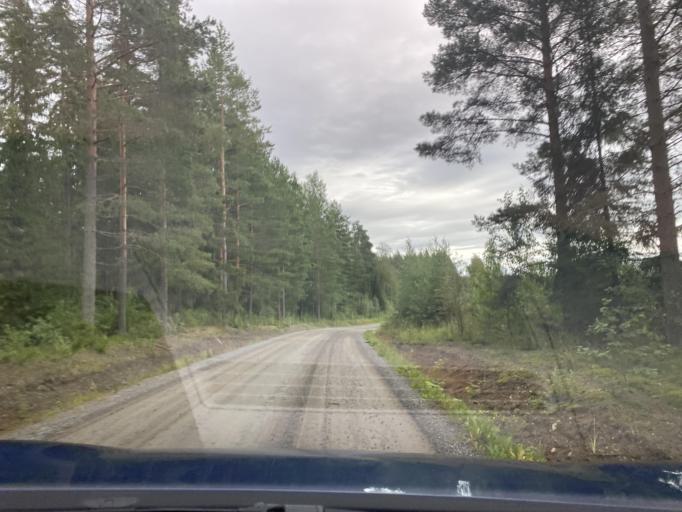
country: FI
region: Pirkanmaa
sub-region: Lounais-Pirkanmaa
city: Punkalaidun
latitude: 61.2485
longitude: 23.0414
